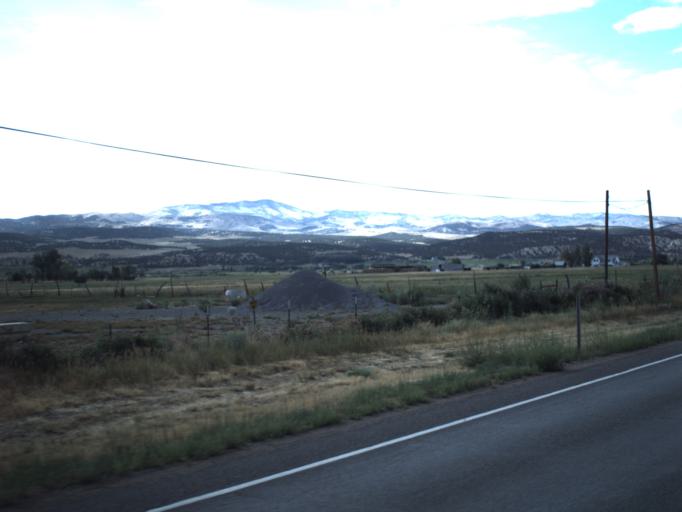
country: US
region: Utah
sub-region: Sanpete County
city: Mount Pleasant
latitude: 39.5571
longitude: -111.4554
